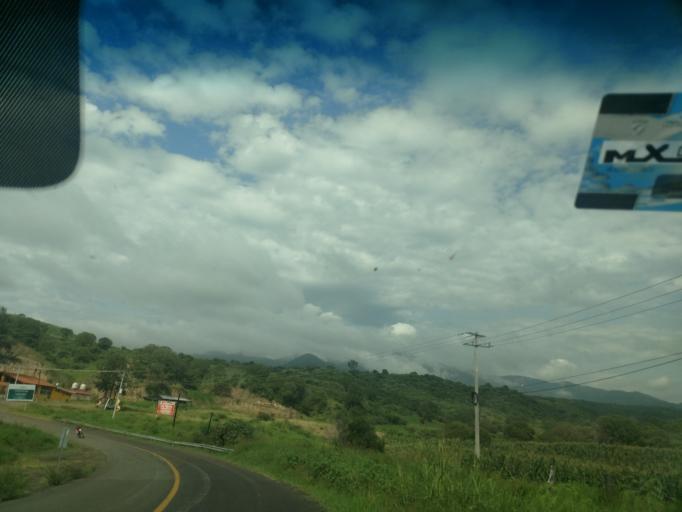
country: MX
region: Jalisco
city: El Salto
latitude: 20.4236
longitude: -104.5000
